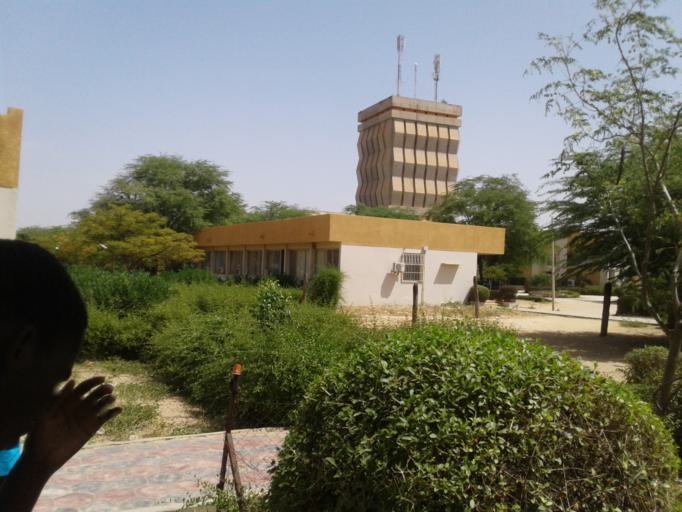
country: SN
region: Saint-Louis
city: Saint-Louis
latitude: 16.0616
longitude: -16.4241
